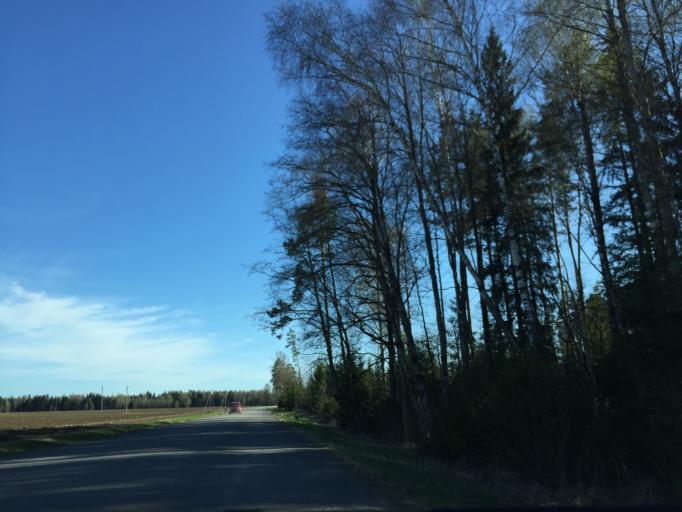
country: EE
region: Valgamaa
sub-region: Valga linn
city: Valga
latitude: 57.8581
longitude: 26.2532
